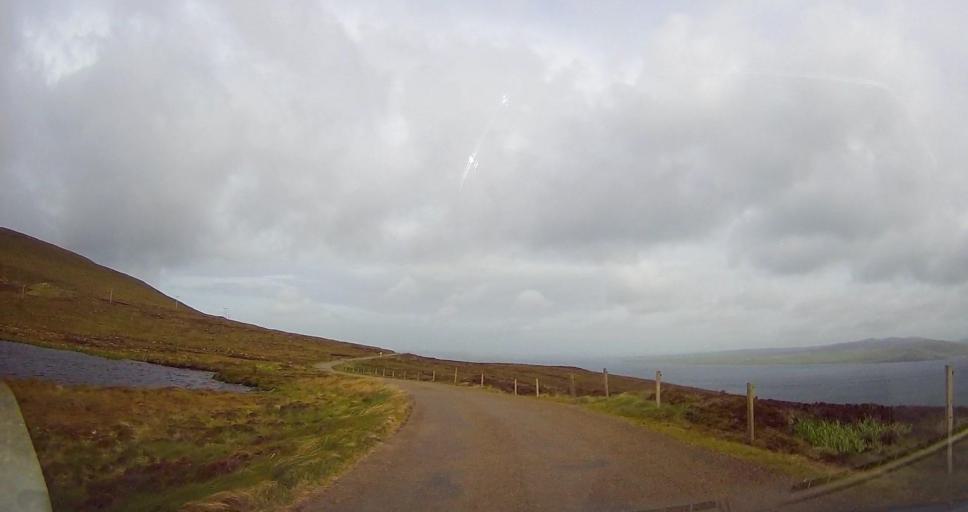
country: GB
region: Scotland
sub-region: Orkney Islands
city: Stromness
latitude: 58.8809
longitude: -3.2478
